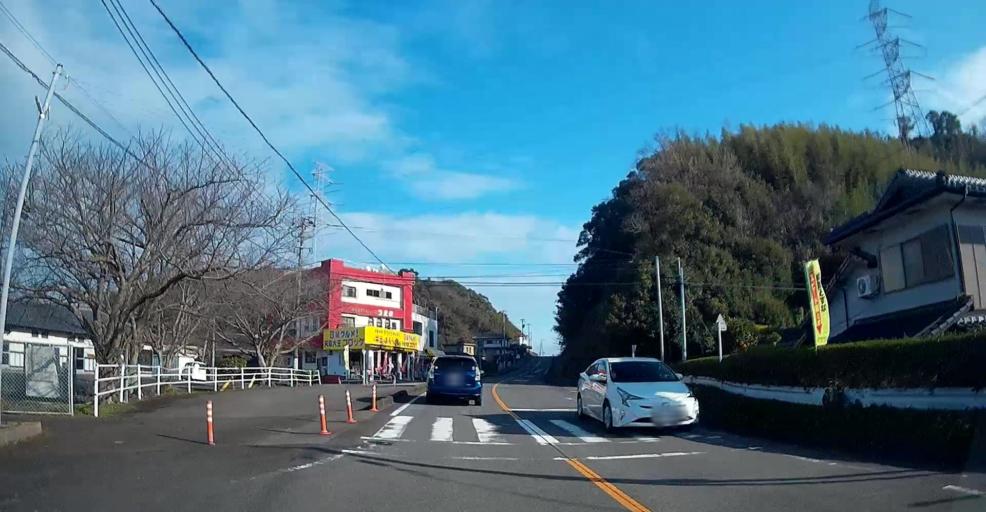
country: JP
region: Kumamoto
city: Yatsushiro
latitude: 32.5180
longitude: 130.4528
